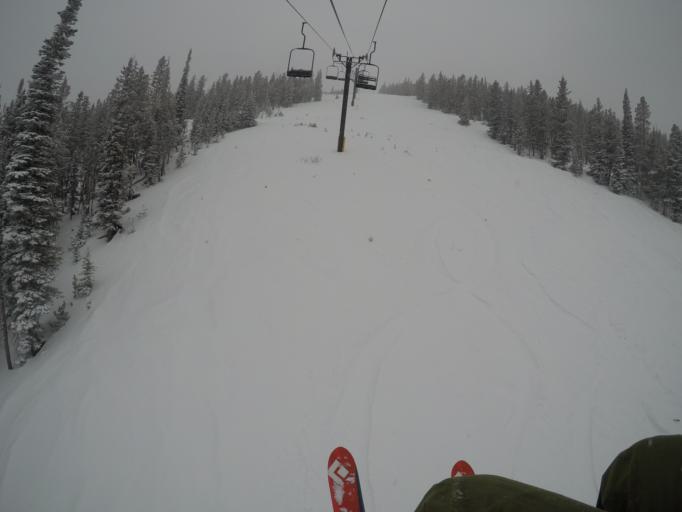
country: US
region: Montana
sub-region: Carbon County
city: Red Lodge
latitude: 45.1867
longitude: -109.3521
